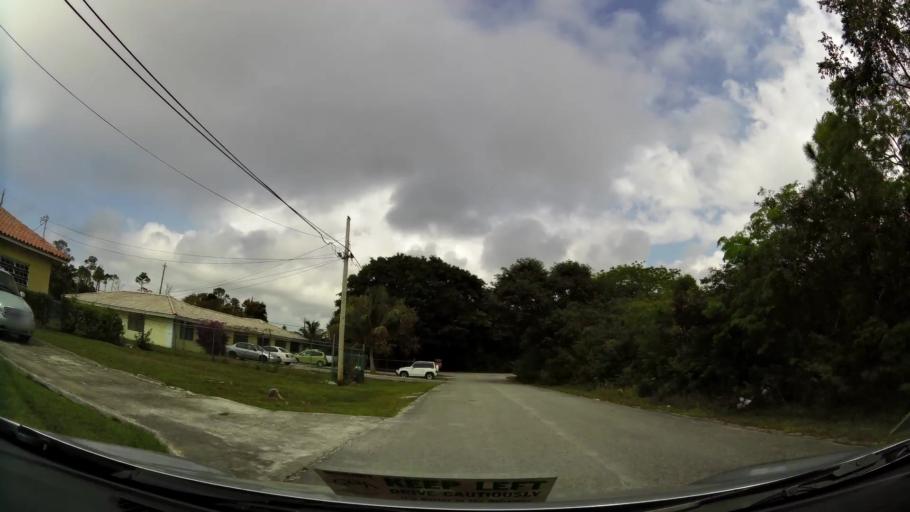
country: BS
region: Freeport
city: Lucaya
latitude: 26.5411
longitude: -78.5967
